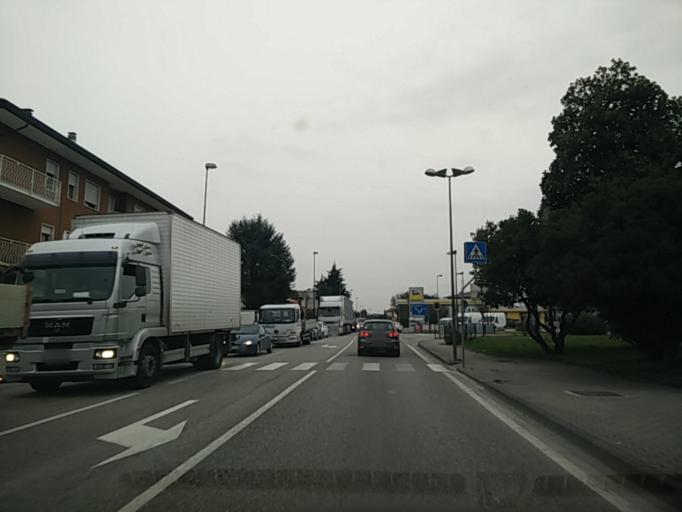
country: IT
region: Veneto
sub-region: Provincia di Venezia
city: Scorze
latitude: 45.5696
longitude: 12.1129
